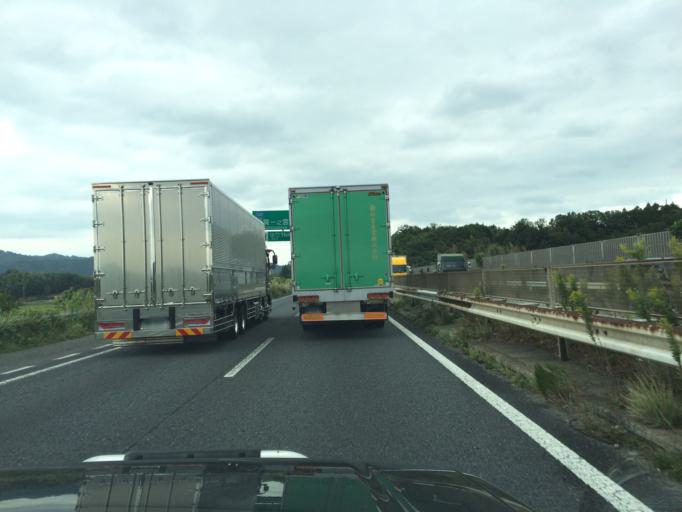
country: JP
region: Mie
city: Ueno-ebisumachi
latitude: 34.7807
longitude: 136.1584
